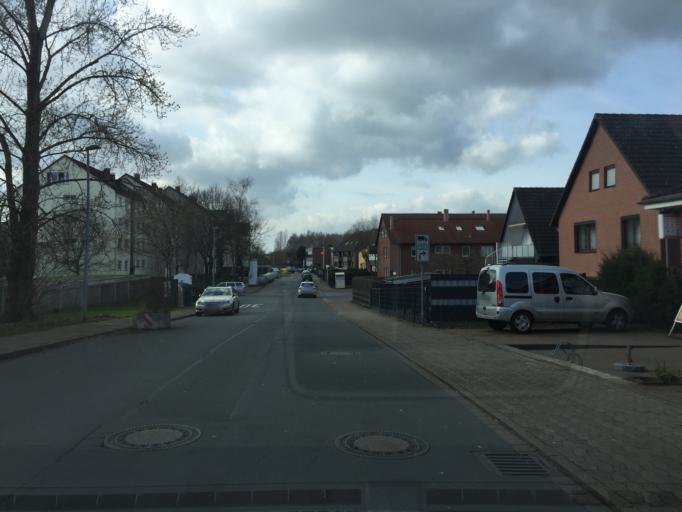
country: DE
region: Lower Saxony
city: Garbsen
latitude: 52.4224
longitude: 9.5862
